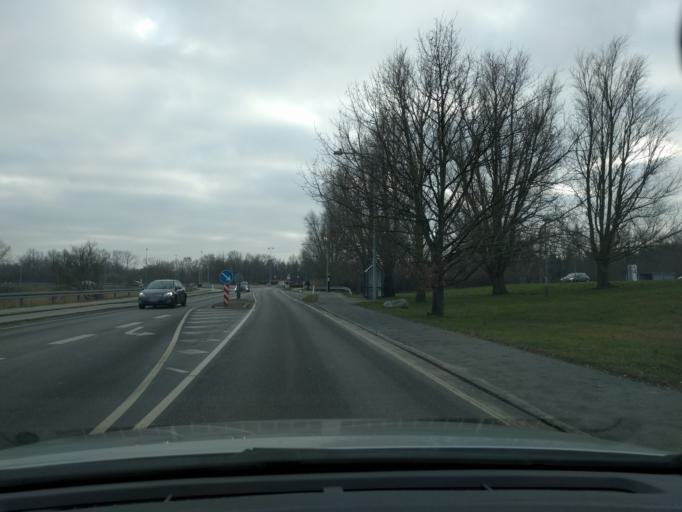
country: DK
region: Zealand
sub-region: Guldborgsund Kommune
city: Nykobing Falster
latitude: 54.7588
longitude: 11.8556
